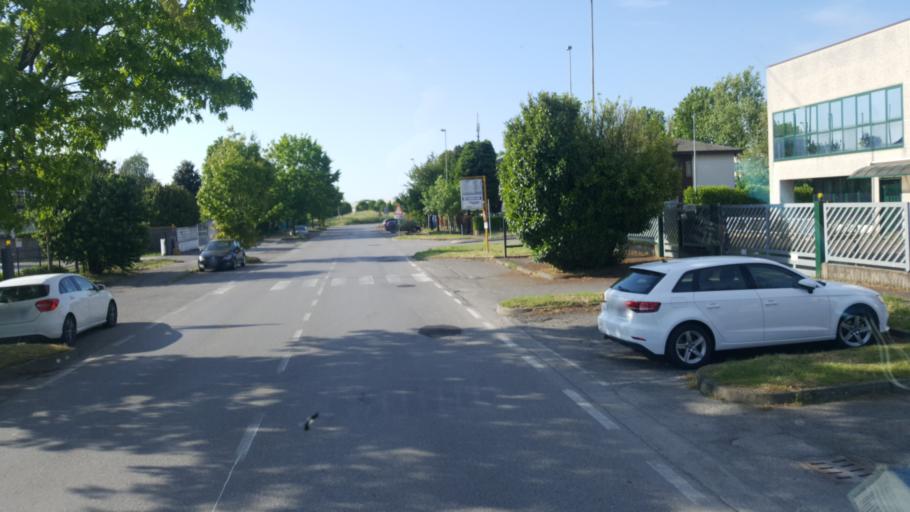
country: IT
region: Lombardy
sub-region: Citta metropolitana di Milano
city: Liscate
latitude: 45.4893
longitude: 9.4088
